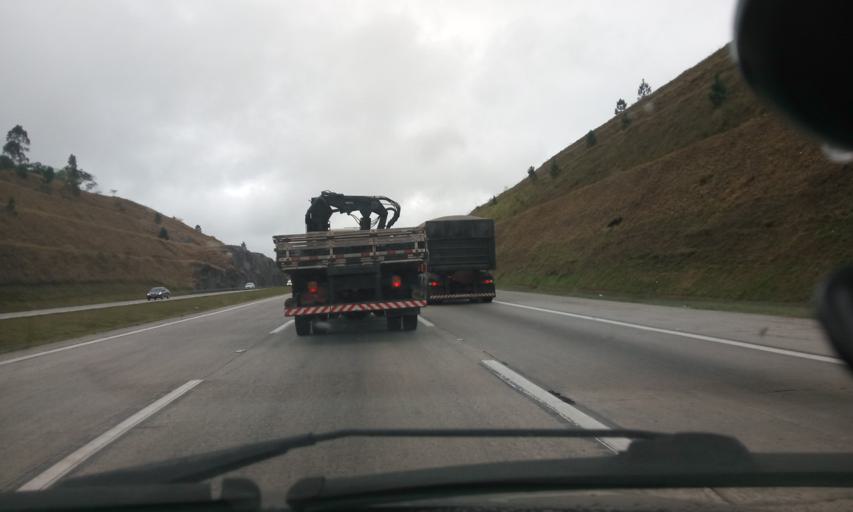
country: BR
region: Sao Paulo
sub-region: Itapecerica Da Serra
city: Itapecerica da Serra
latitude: -23.7513
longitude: -46.8019
